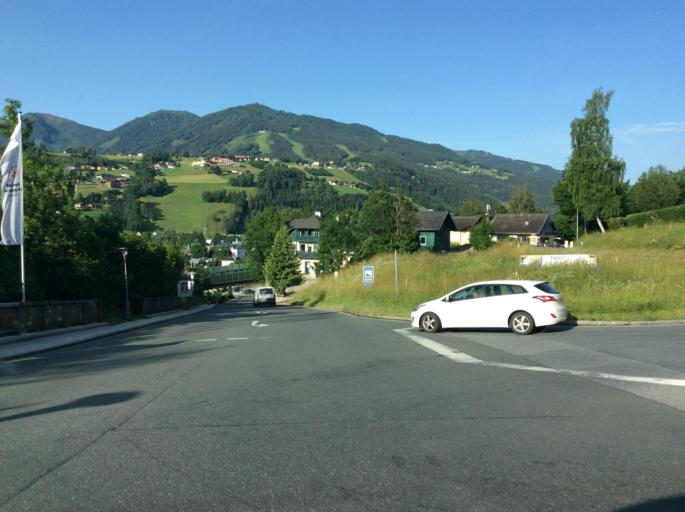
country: AT
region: Styria
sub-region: Politischer Bezirk Liezen
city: Schladming
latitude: 47.3977
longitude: 13.6860
